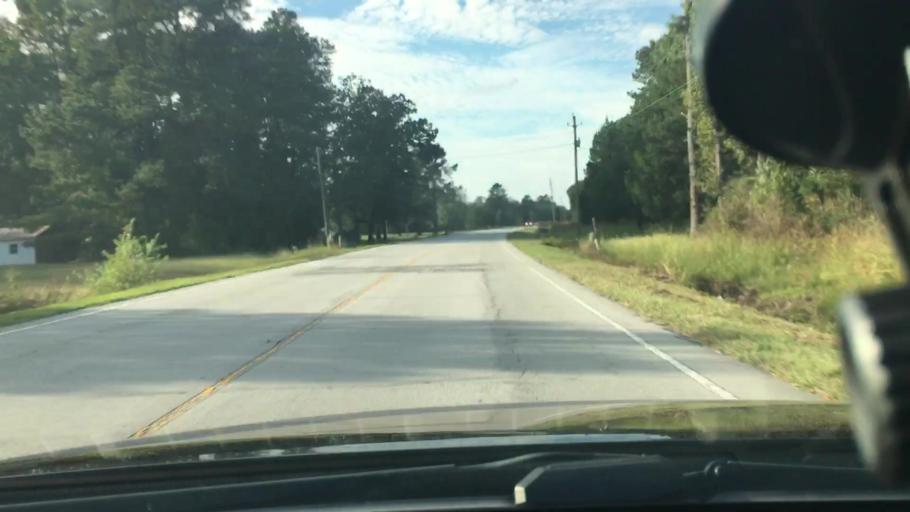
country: US
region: North Carolina
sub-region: Craven County
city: Vanceboro
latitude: 35.3836
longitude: -77.2253
